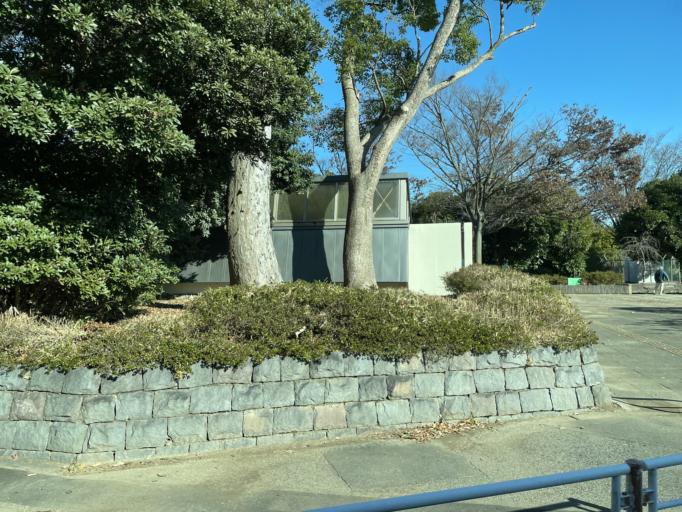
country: JP
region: Saitama
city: Kukichuo
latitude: 36.0704
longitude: 139.6960
